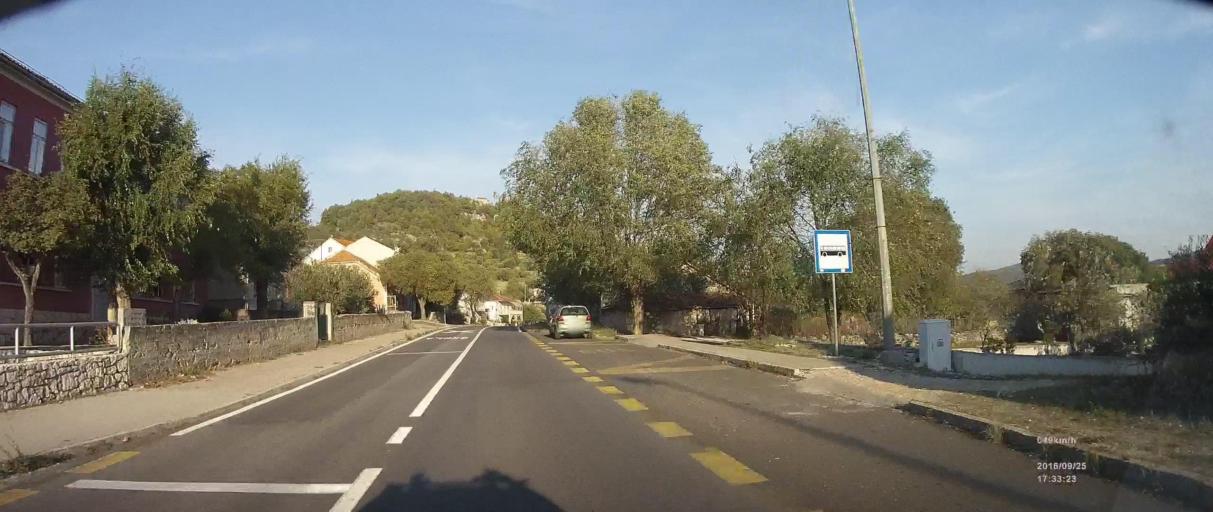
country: HR
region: Sibensko-Kniniska
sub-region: Grad Sibenik
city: Brodarica
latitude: 43.6753
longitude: 16.0123
